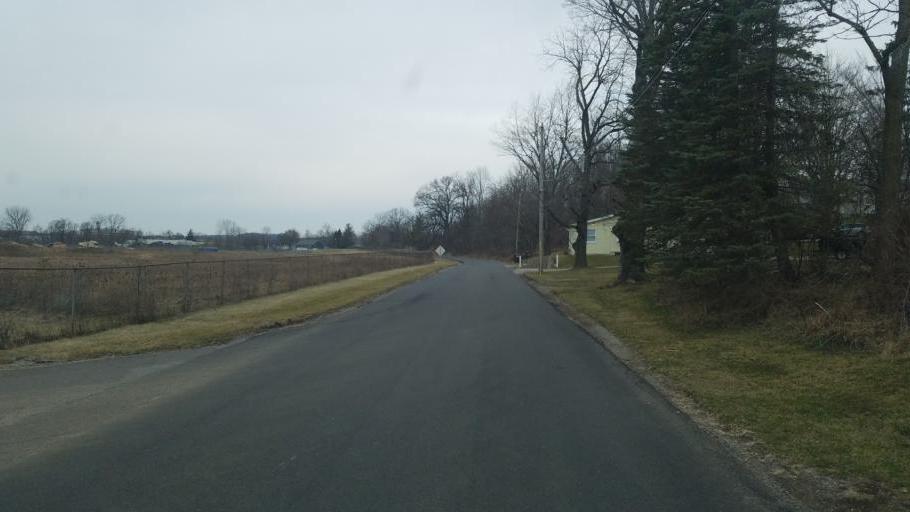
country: US
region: Ohio
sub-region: Richland County
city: Lincoln Heights
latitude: 40.7541
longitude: -82.4887
